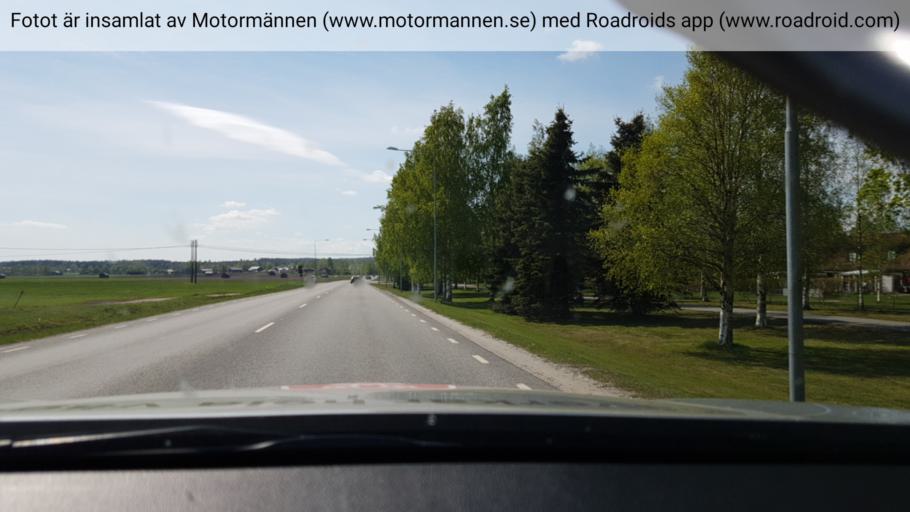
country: SE
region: Vaesterbotten
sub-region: Umea Kommun
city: Roback
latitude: 63.8148
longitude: 20.2192
